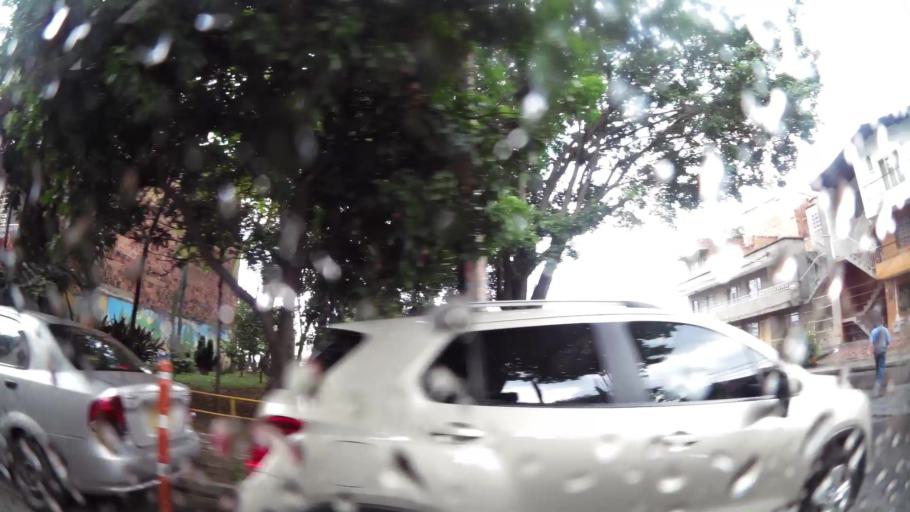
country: CO
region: Antioquia
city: Itagui
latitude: 6.1856
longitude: -75.5942
